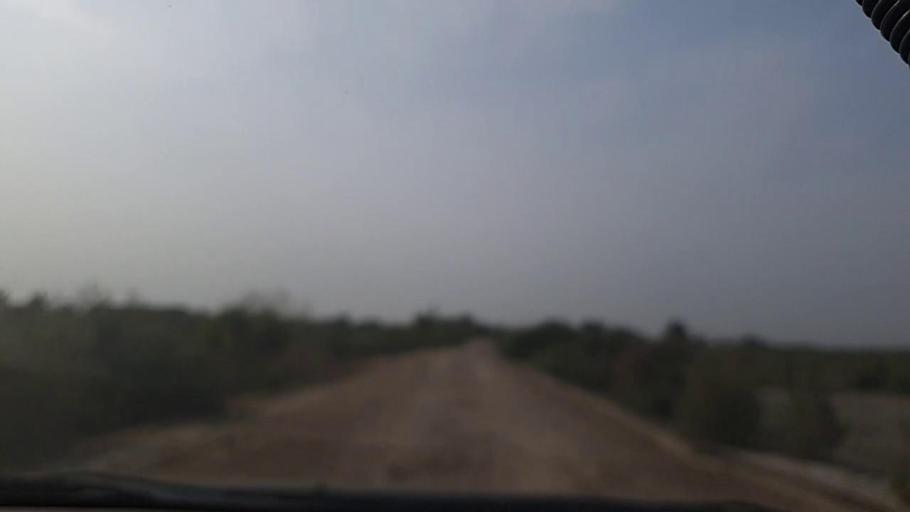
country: PK
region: Sindh
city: Thatta
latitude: 24.6137
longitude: 67.9496
